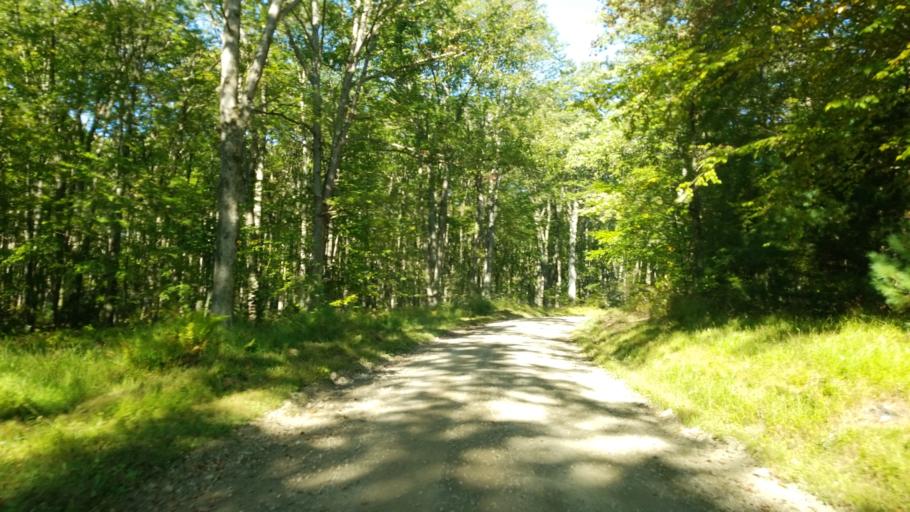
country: US
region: Pennsylvania
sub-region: Clearfield County
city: Curwensville
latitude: 41.1137
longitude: -78.5704
